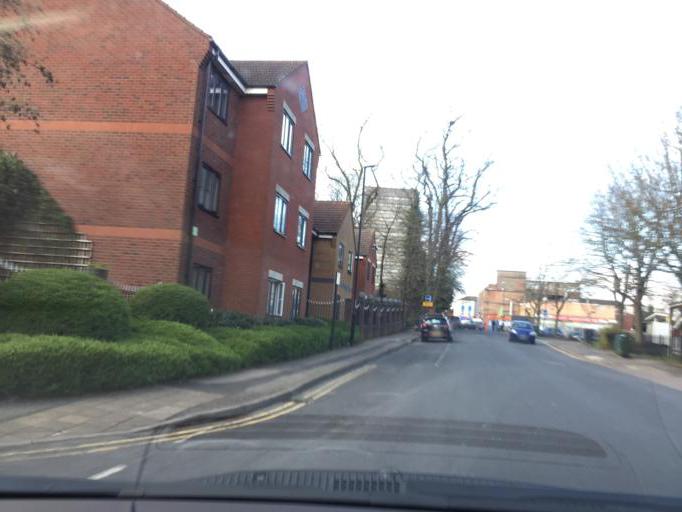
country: GB
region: England
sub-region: Coventry
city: Coventry
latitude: 52.4119
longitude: -1.4998
